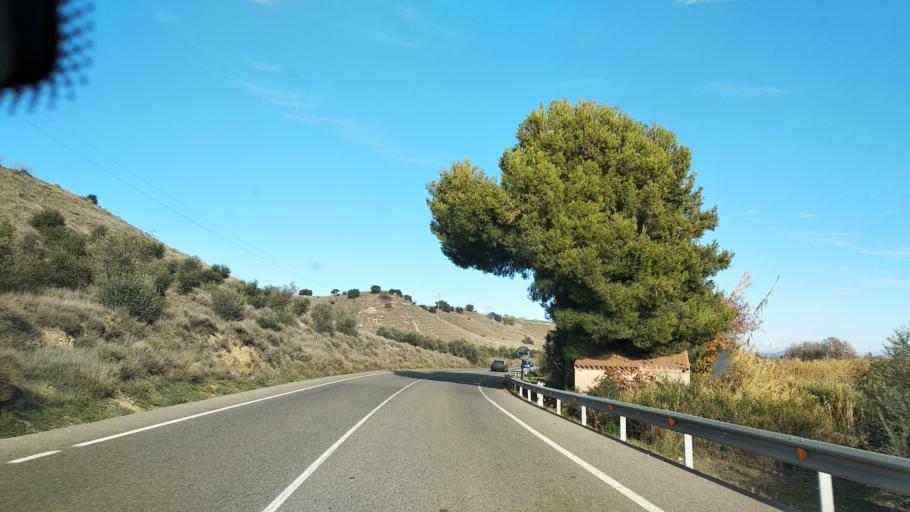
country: ES
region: Catalonia
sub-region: Provincia de Lleida
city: Vallfogona de Balaguer
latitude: 41.7595
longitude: 0.7744
